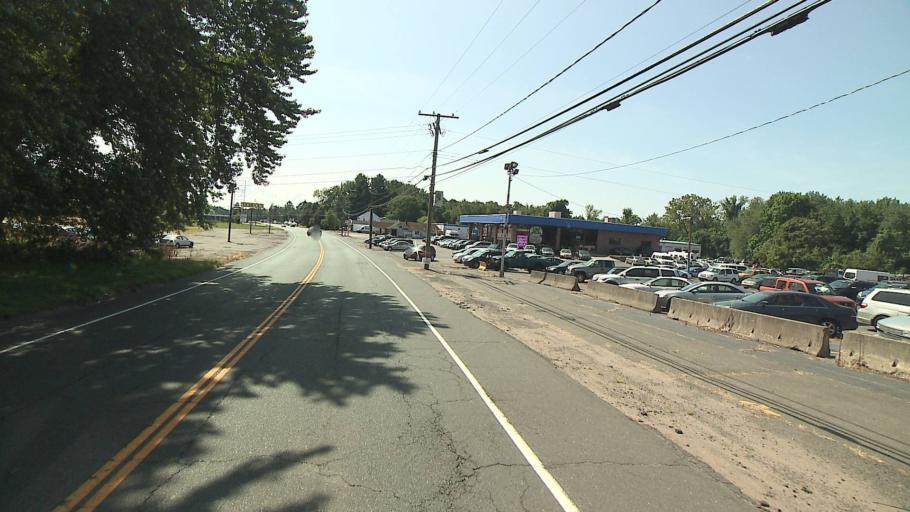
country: US
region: Connecticut
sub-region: Hartford County
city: Windsor
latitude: 41.8763
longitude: -72.6095
